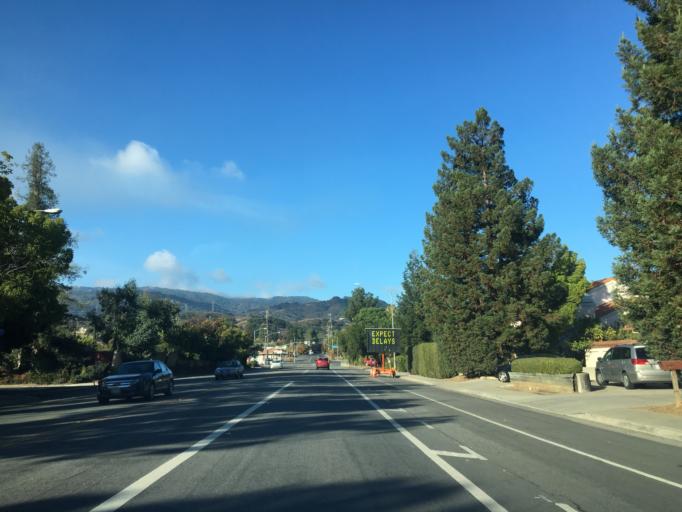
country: US
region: California
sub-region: Santa Clara County
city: Cupertino
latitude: 37.3220
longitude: -122.0662
